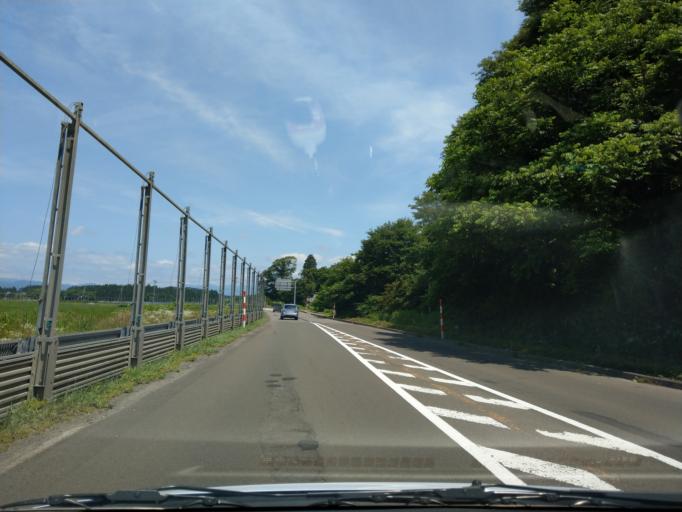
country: JP
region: Akita
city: Takanosu
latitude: 40.1899
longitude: 140.4007
